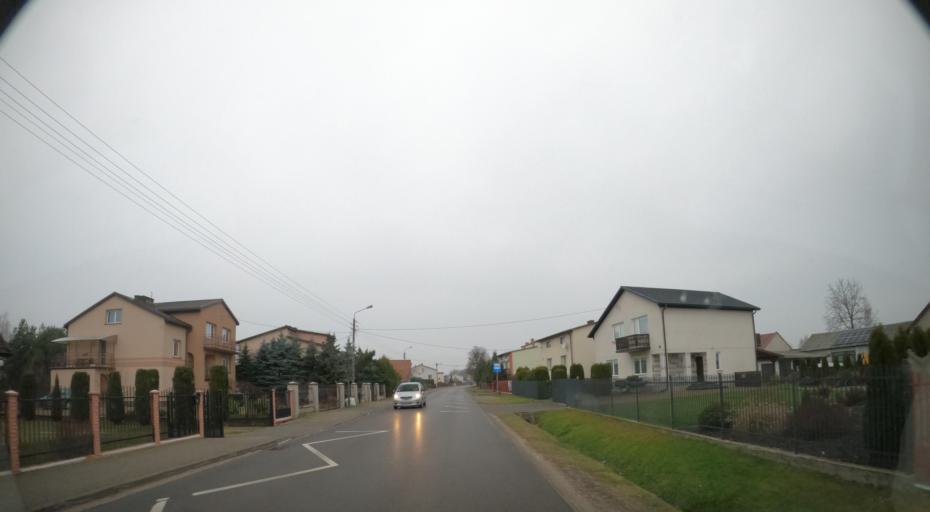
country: PL
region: Masovian Voivodeship
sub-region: Powiat radomski
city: Skaryszew
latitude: 51.3805
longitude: 21.2270
